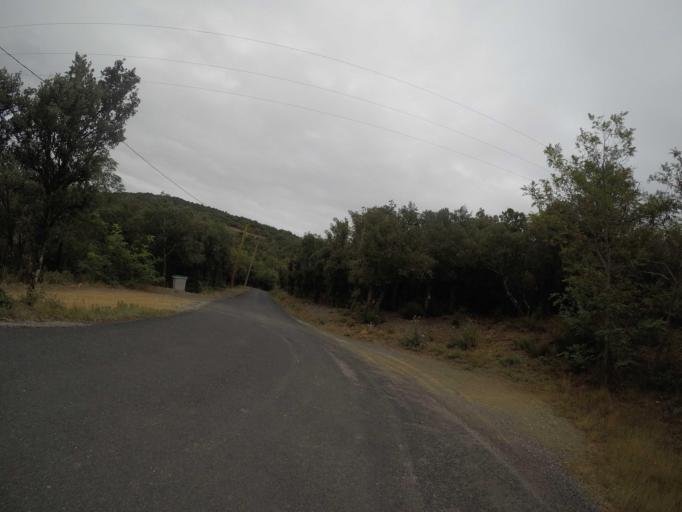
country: FR
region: Languedoc-Roussillon
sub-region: Departement des Pyrenees-Orientales
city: Ille-sur-Tet
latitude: 42.6143
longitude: 2.6187
